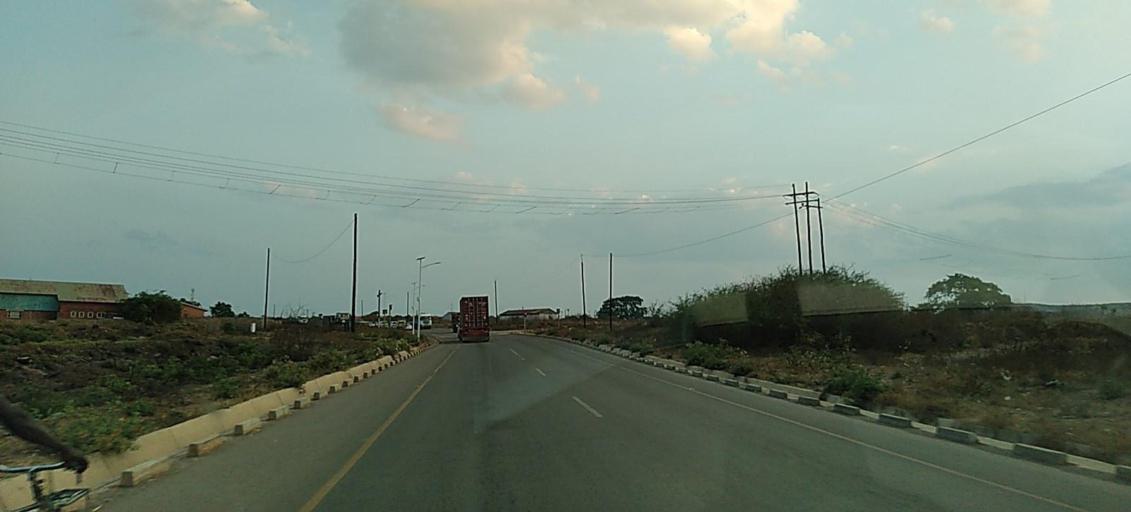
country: ZM
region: Copperbelt
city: Chingola
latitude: -12.5366
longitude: 27.8392
